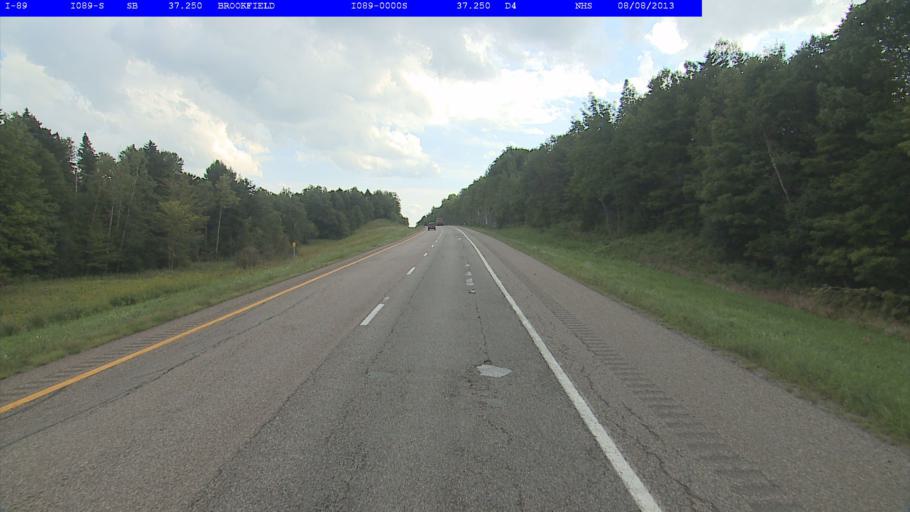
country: US
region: Vermont
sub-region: Orange County
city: Williamstown
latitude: 44.0359
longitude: -72.6143
